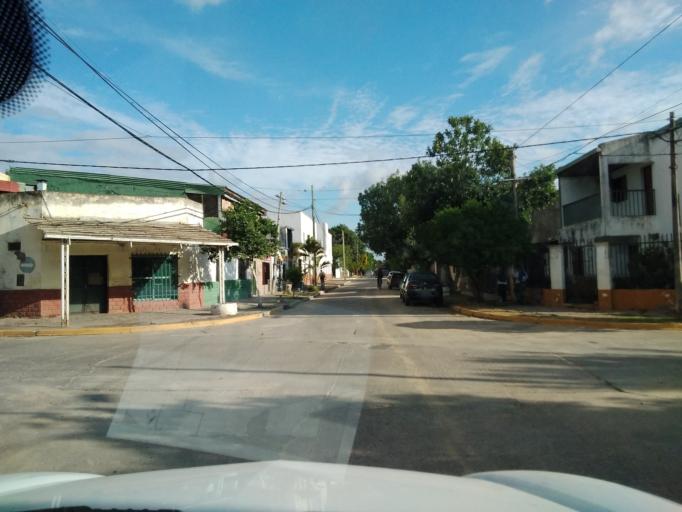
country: AR
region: Corrientes
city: Corrientes
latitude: -27.4616
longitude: -58.8192
